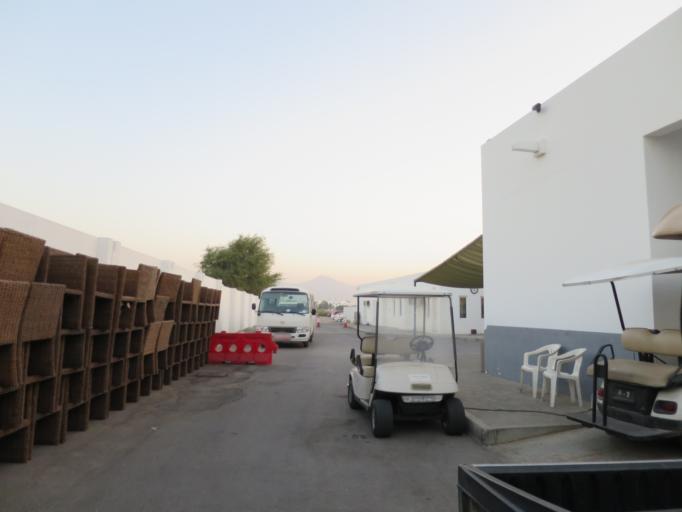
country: OM
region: Muhafazat Masqat
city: Bawshar
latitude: 23.6021
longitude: 58.4001
